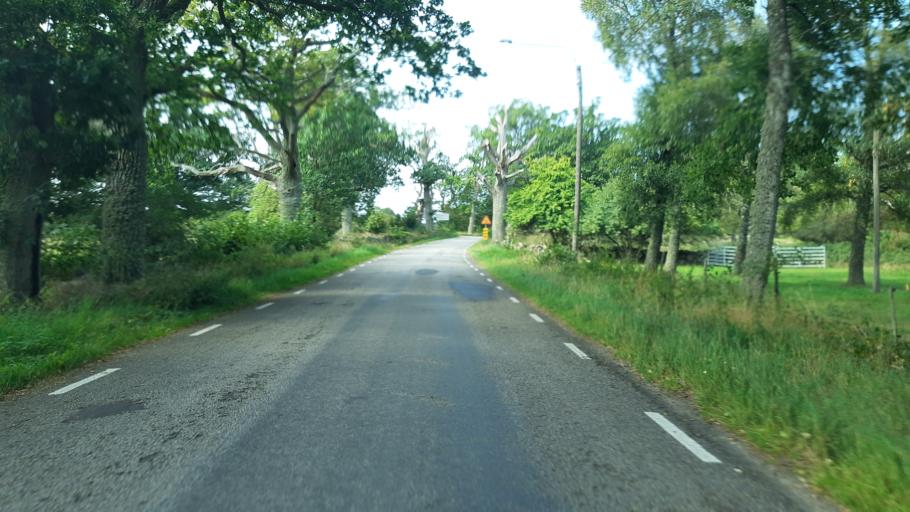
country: SE
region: Blekinge
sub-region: Karlskrona Kommun
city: Nattraby
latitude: 56.2254
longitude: 15.4258
